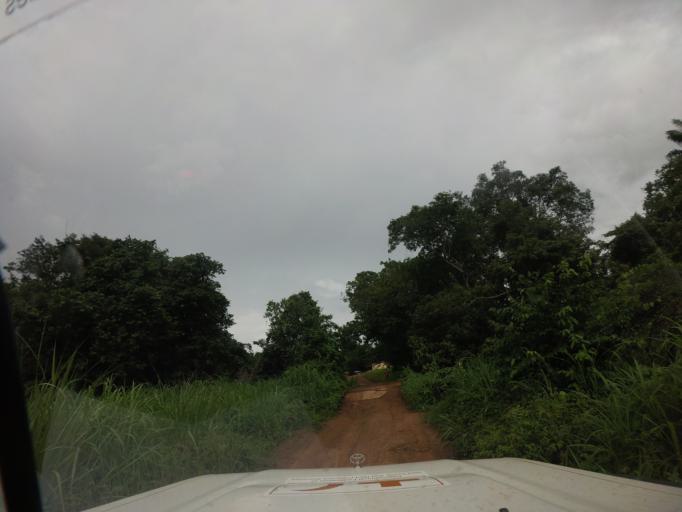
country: SL
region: Northern Province
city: Loma
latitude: 9.8460
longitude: -12.3799
